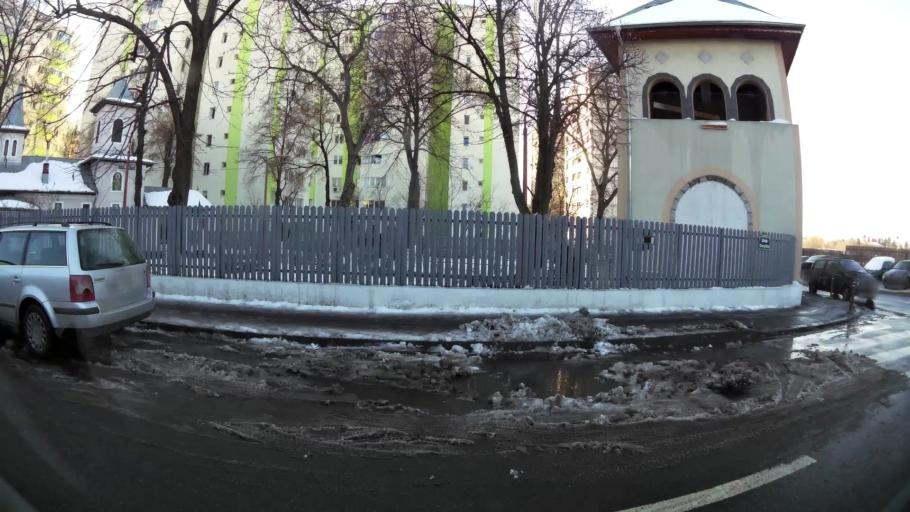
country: RO
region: Ilfov
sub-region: Comuna Fundeni-Dobroesti
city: Fundeni
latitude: 44.4702
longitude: 26.1417
